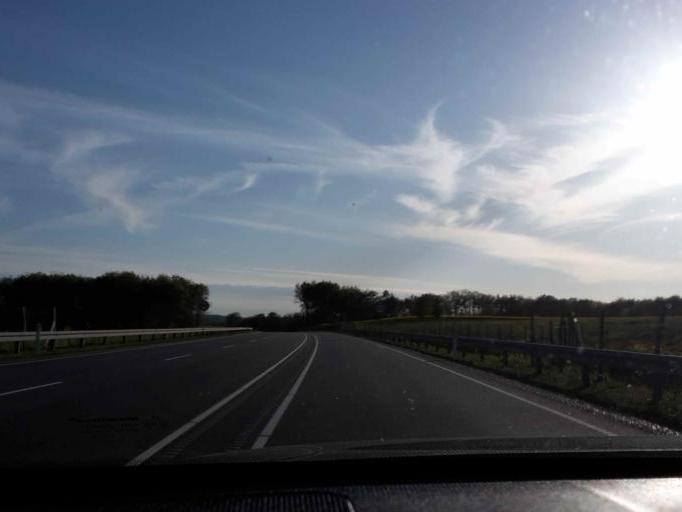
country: DK
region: Central Jutland
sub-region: Randers Kommune
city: Assentoft
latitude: 56.4311
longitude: 10.1304
